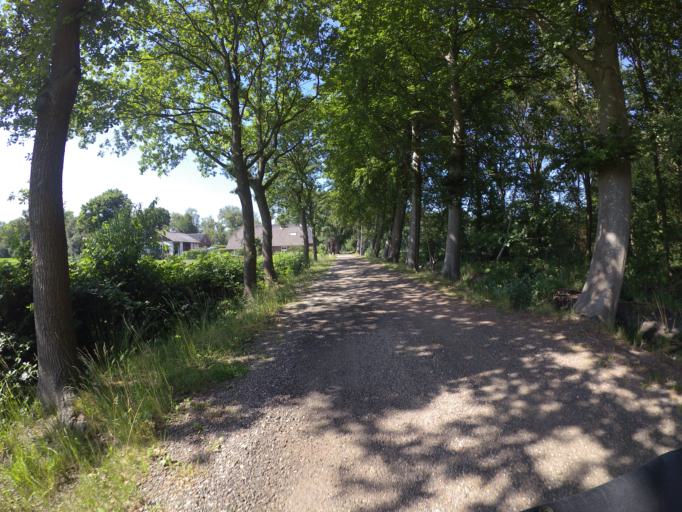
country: NL
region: North Brabant
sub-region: Gemeente Heusden
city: Heusden
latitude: 51.7011
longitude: 5.1616
